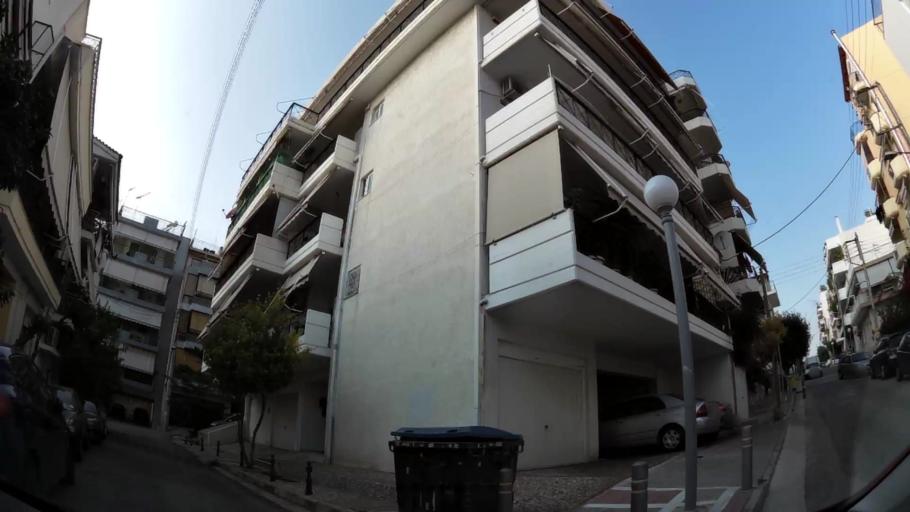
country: GR
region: Attica
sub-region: Nomarchia Athinas
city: Dhafni
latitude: 37.9499
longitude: 23.7286
